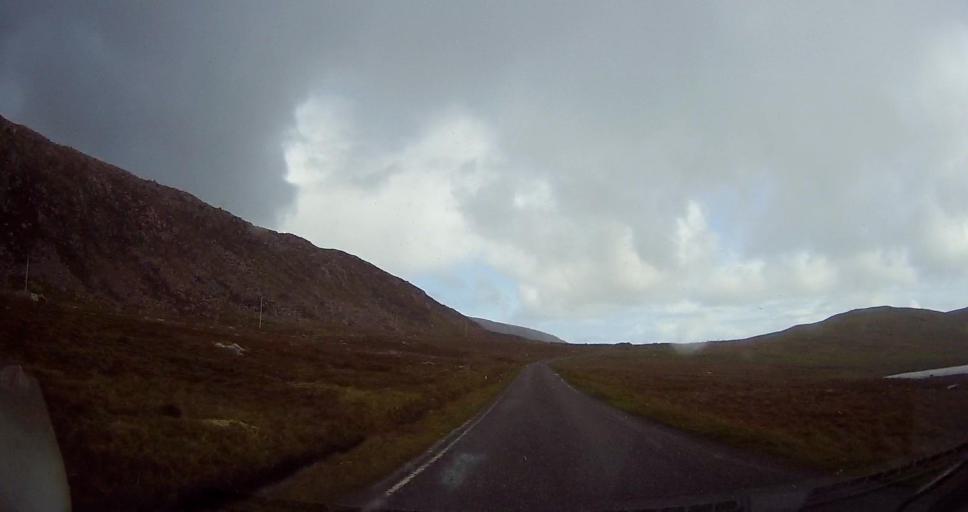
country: GB
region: Scotland
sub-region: Shetland Islands
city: Lerwick
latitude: 60.5501
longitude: -1.3405
